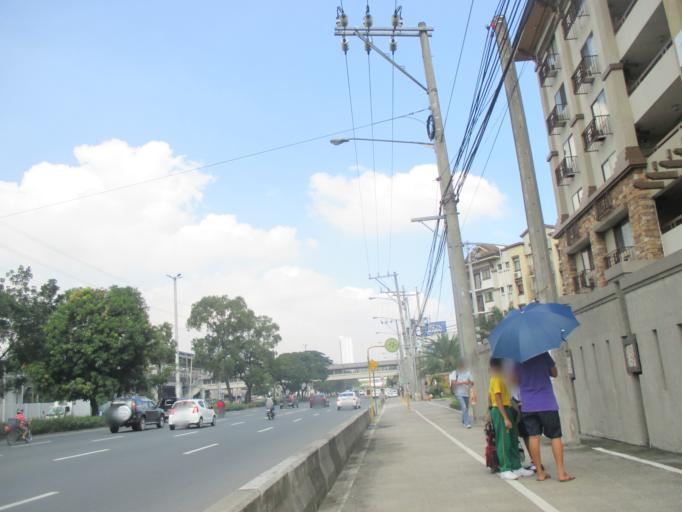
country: PH
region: Metro Manila
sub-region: Marikina
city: Calumpang
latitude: 14.6210
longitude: 121.0879
